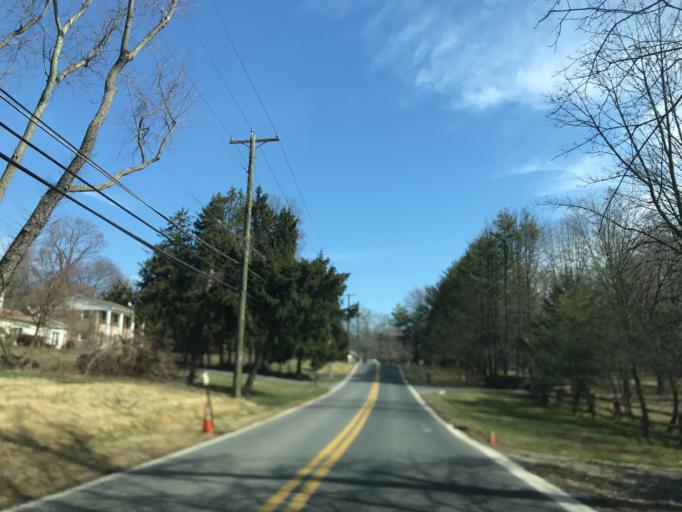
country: US
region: Maryland
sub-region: Montgomery County
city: Ashton-Sandy Spring
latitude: 39.1376
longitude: -76.9911
